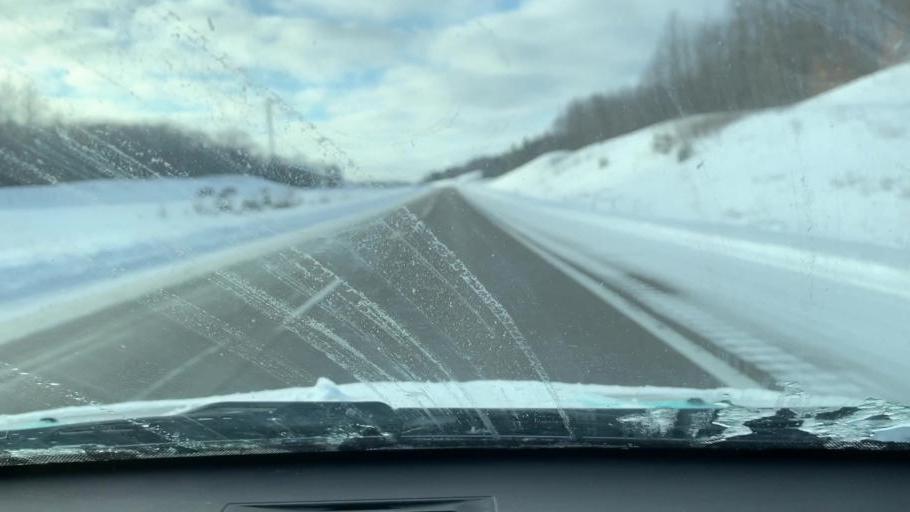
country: US
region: Michigan
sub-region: Wexford County
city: Manton
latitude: 44.3405
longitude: -85.4058
